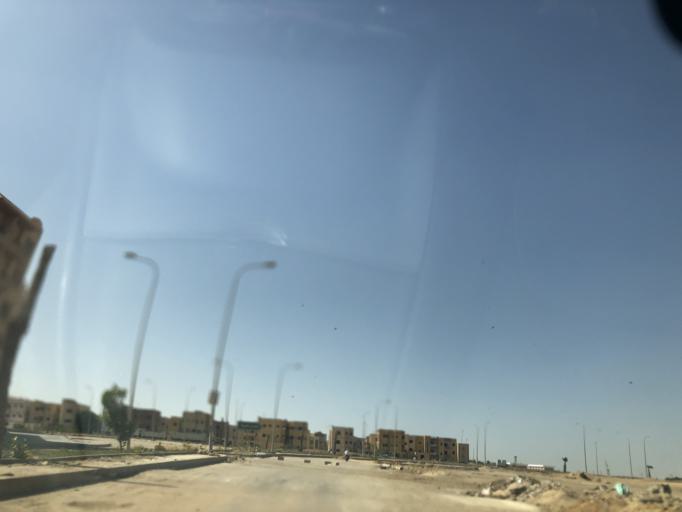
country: EG
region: Al Jizah
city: Madinat Sittah Uktubar
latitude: 29.9272
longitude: 31.0372
